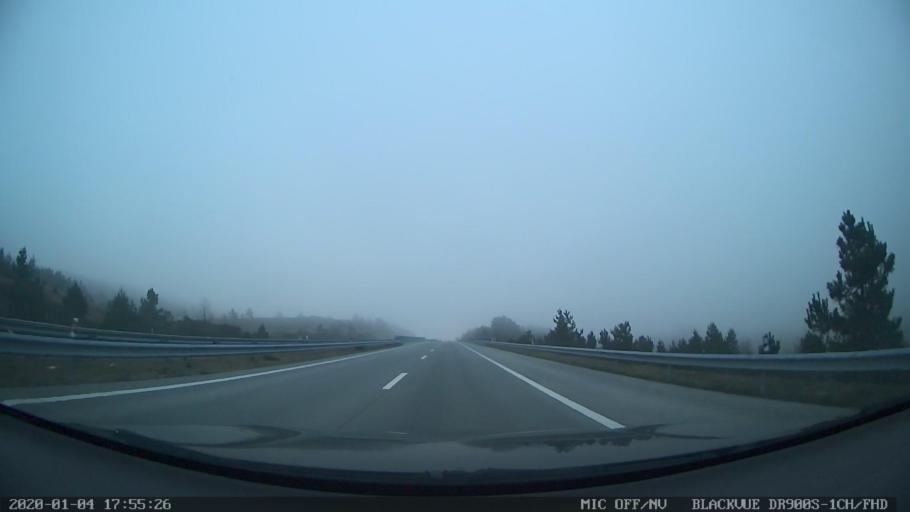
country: PT
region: Vila Real
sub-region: Ribeira de Pena
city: Ribeira de Pena
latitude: 41.5062
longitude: -7.7292
